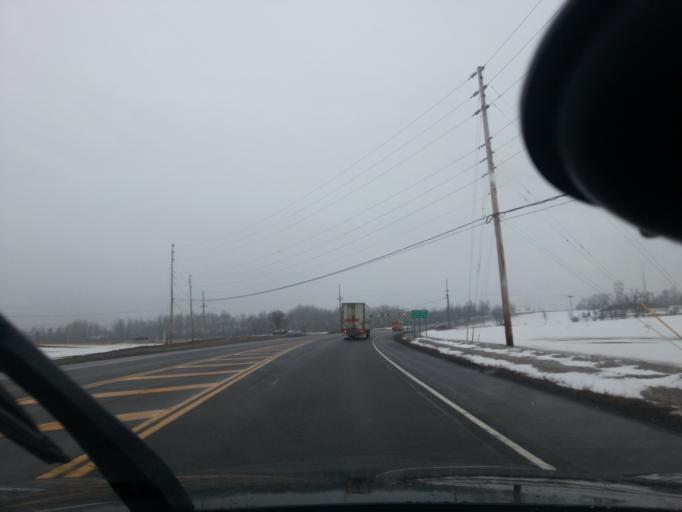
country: US
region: New York
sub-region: Jefferson County
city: Fort Drum
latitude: 44.0850
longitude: -75.7954
